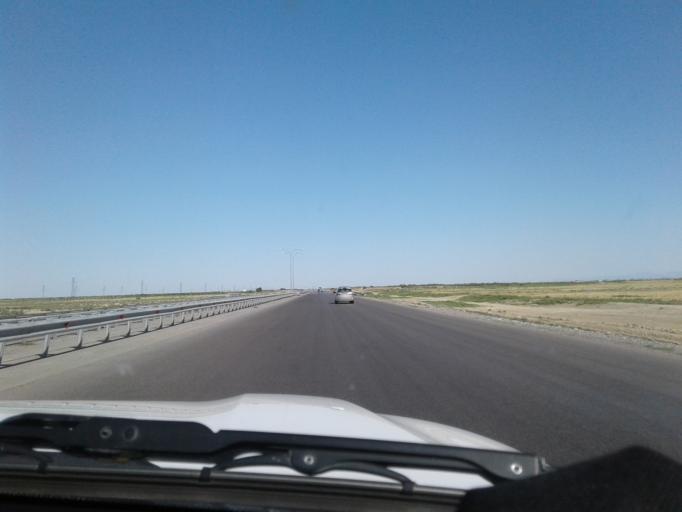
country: IR
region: Razavi Khorasan
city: Dargaz
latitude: 37.5786
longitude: 59.3159
